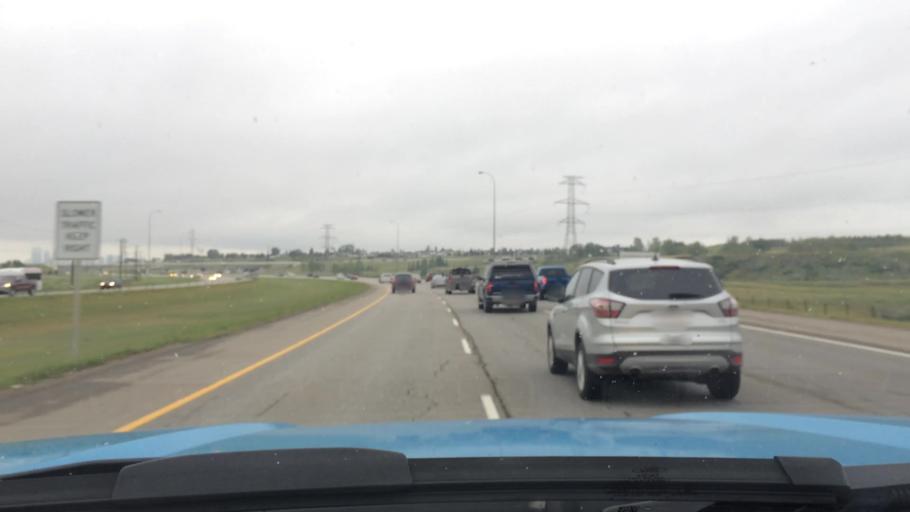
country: CA
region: Alberta
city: Calgary
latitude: 51.1335
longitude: -114.0435
